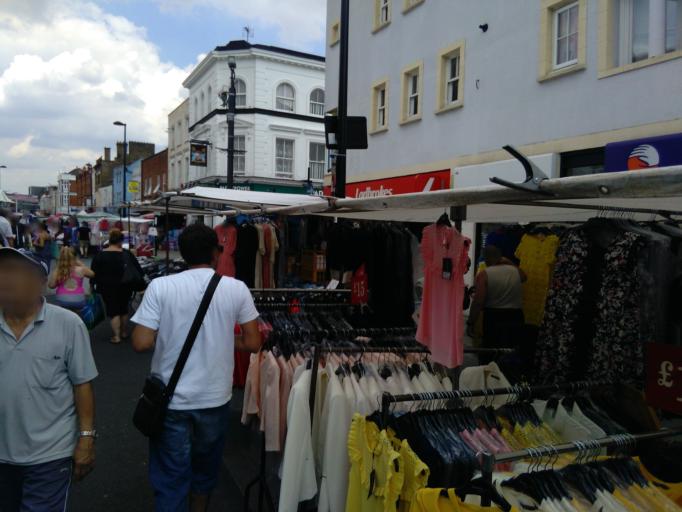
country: GB
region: England
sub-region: Greater London
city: Catford
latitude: 51.4759
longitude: -0.0259
